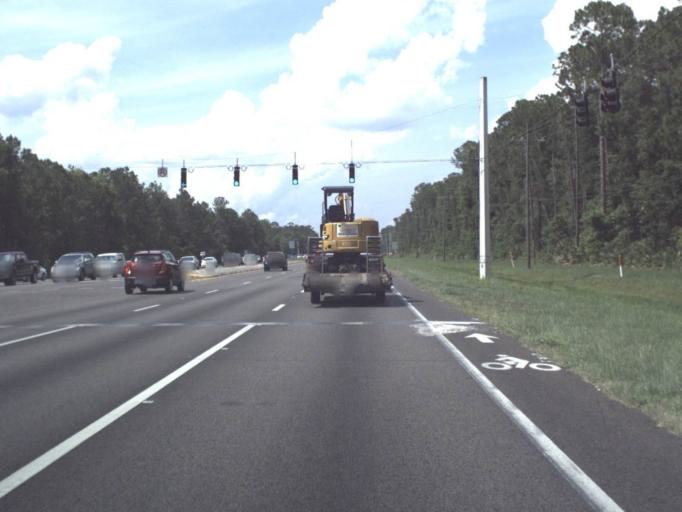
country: US
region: Florida
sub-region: Saint Johns County
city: Fruit Cove
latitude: 30.0969
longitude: -81.7058
